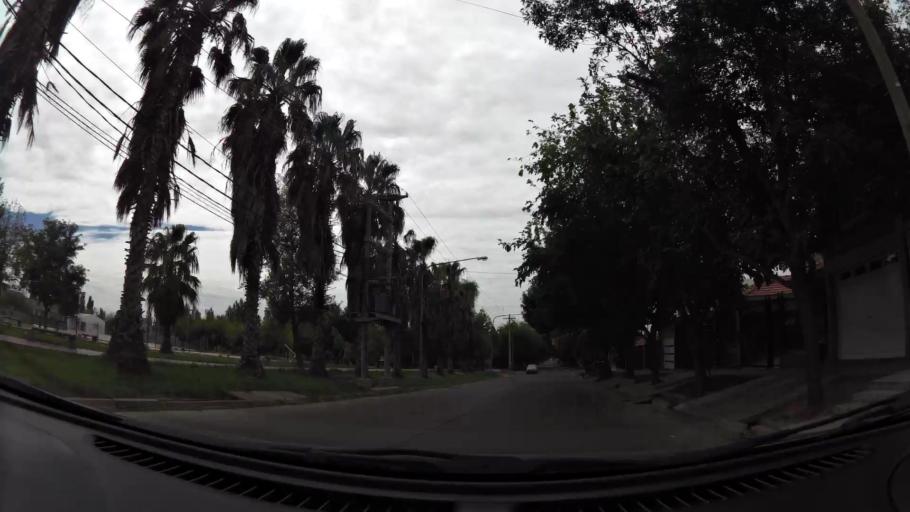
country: AR
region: Mendoza
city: Las Heras
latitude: -32.8589
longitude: -68.8555
